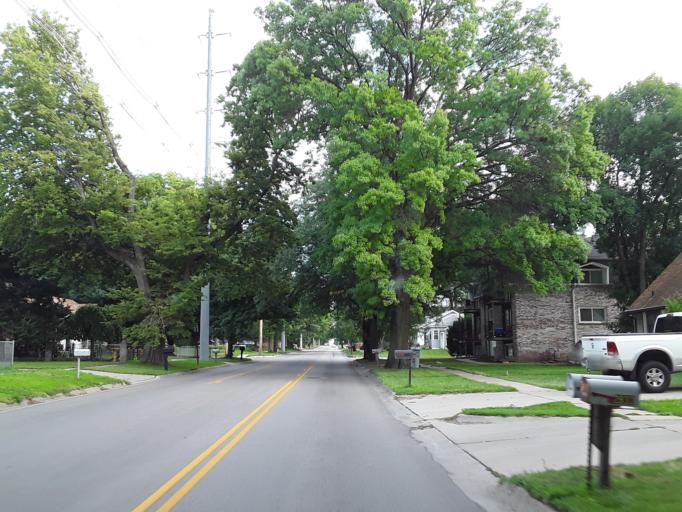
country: US
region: Nebraska
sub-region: Lancaster County
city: Lincoln
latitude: 40.8422
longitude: -96.6442
